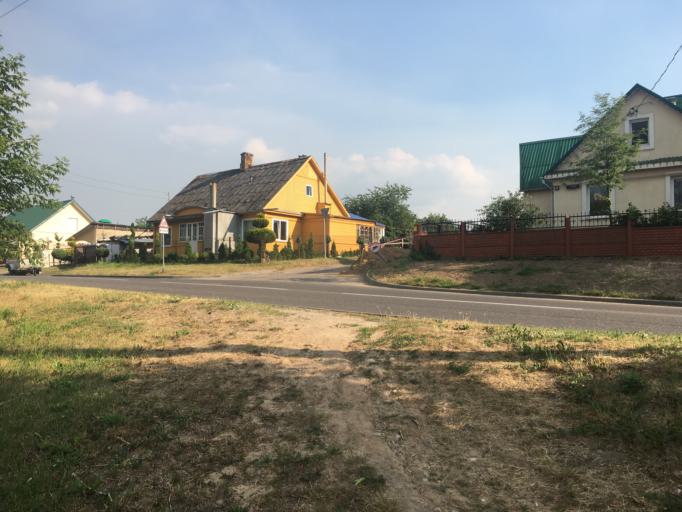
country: BY
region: Grodnenskaya
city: Hrodna
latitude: 53.6659
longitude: 23.8158
